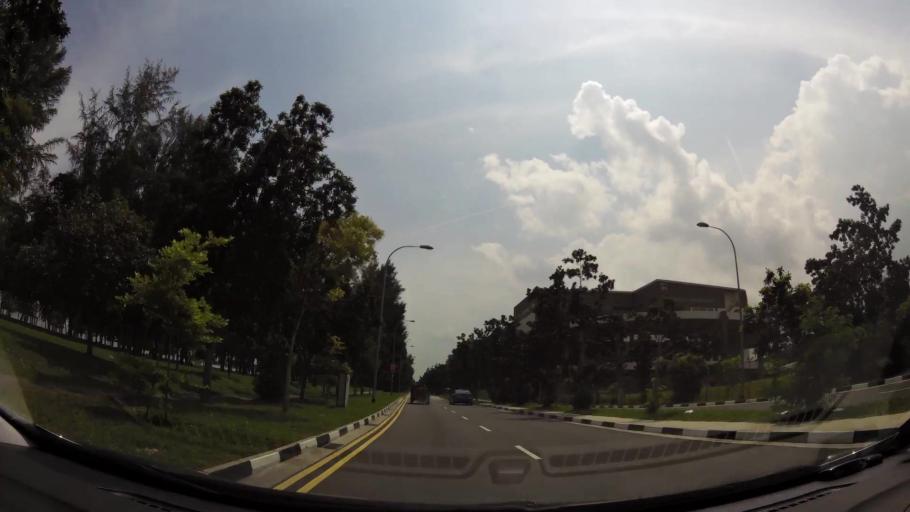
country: MY
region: Johor
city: Kampung Pasir Gudang Baru
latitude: 1.3832
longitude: 104.0011
